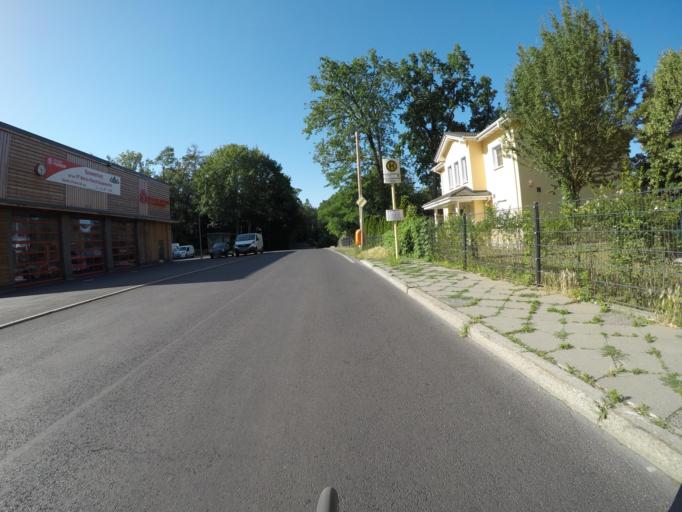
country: DE
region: Berlin
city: Schmockwitz
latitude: 52.3474
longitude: 13.6455
